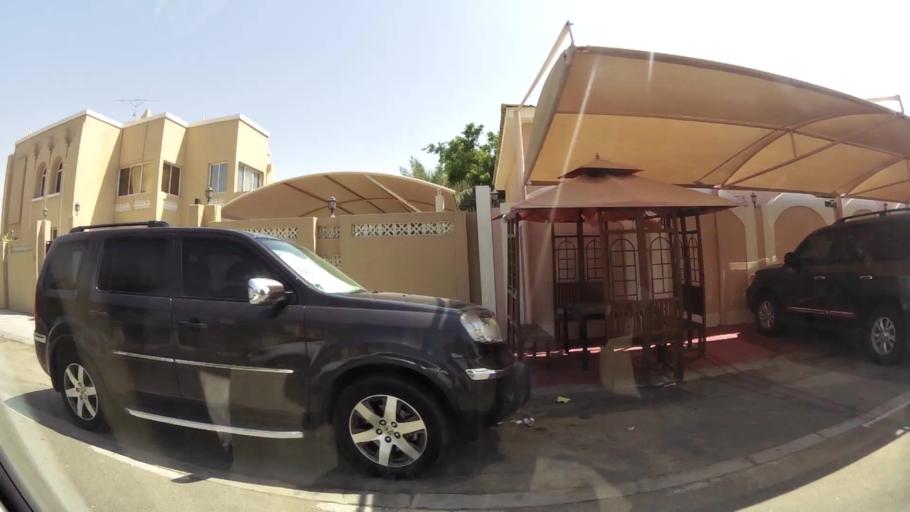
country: AE
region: Ash Shariqah
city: Sharjah
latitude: 25.2732
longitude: 55.3664
